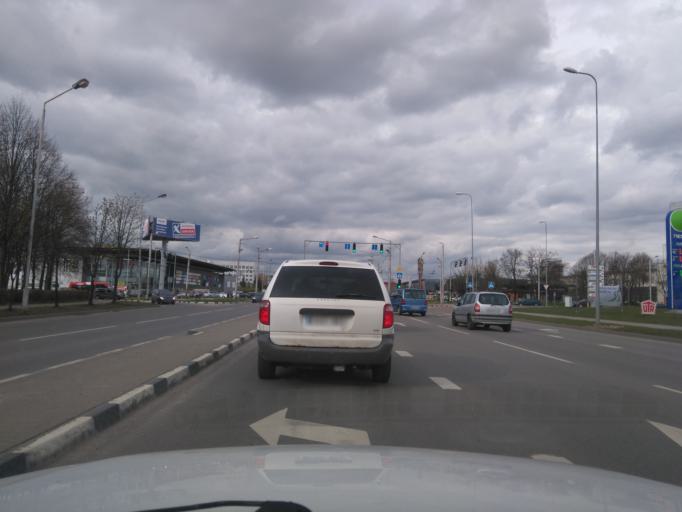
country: LT
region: Kauno apskritis
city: Dainava (Kaunas)
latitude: 54.9101
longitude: 23.9830
